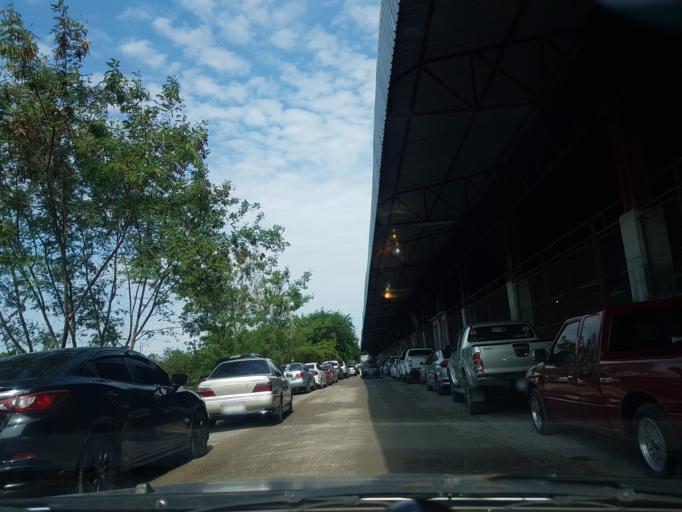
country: TH
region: Sara Buri
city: Phra Phutthabat
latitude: 14.7469
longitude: 100.7469
